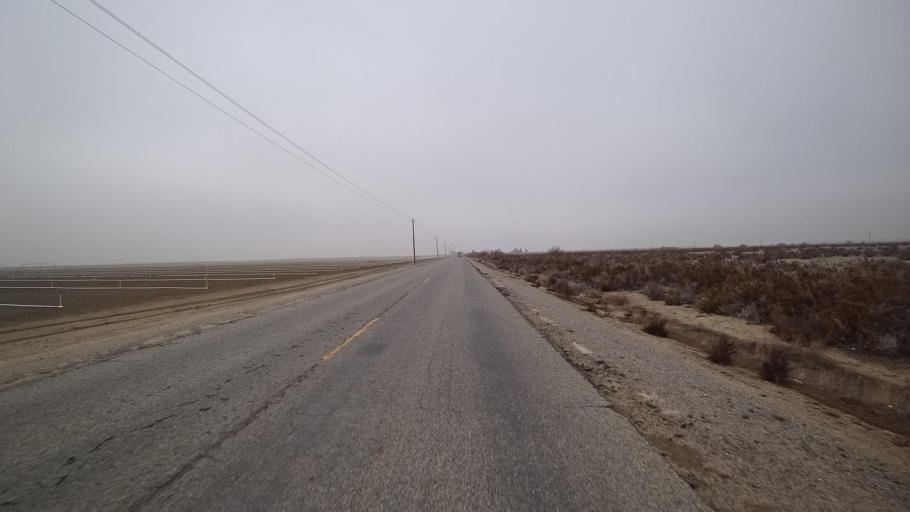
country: US
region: California
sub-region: Kern County
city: Maricopa
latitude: 35.1520
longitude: -119.2180
